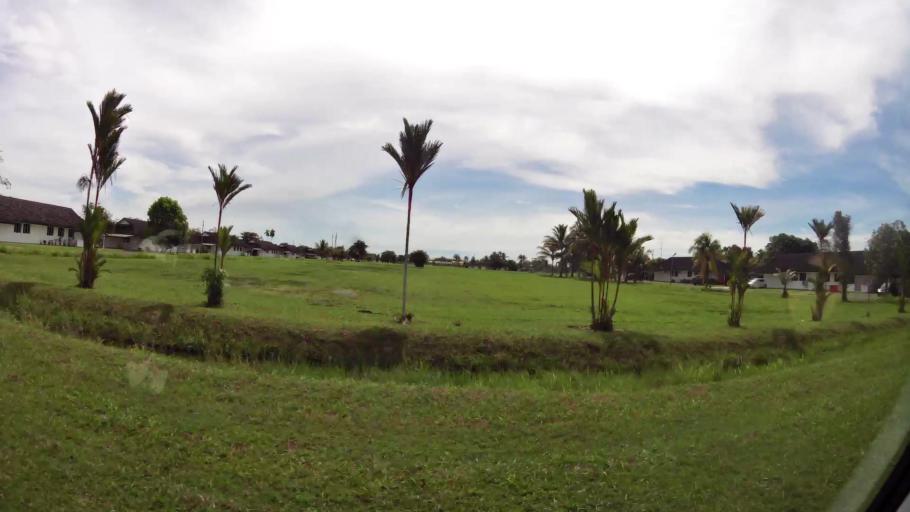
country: BN
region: Belait
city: Seria
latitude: 4.6074
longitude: 114.3204
